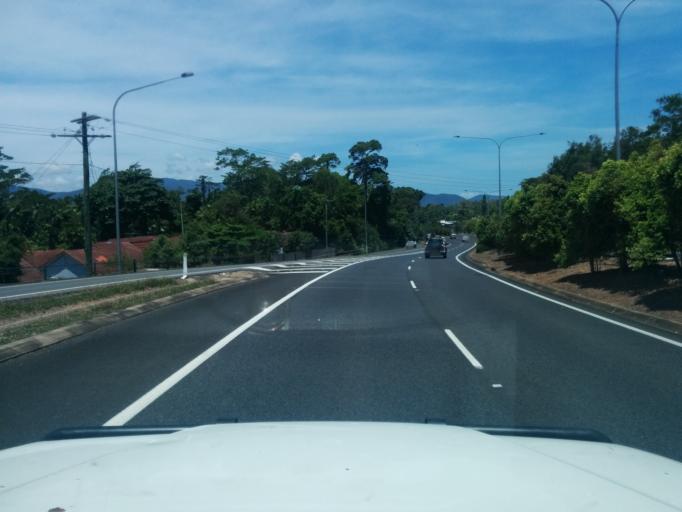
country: AU
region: Queensland
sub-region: Cairns
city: Cairns
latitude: -16.9148
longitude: 145.7295
